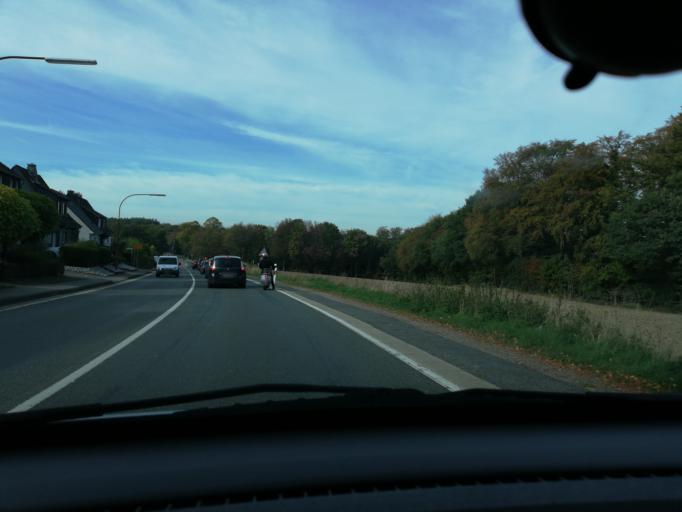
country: DE
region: North Rhine-Westphalia
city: Sprockhovel
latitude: 51.3310
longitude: 7.2644
